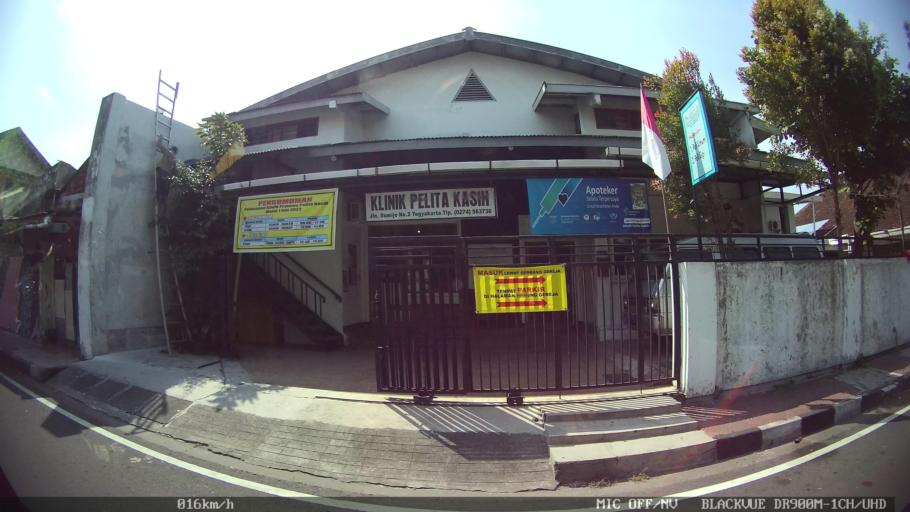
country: ID
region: Daerah Istimewa Yogyakarta
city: Yogyakarta
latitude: -7.7877
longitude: 110.3625
